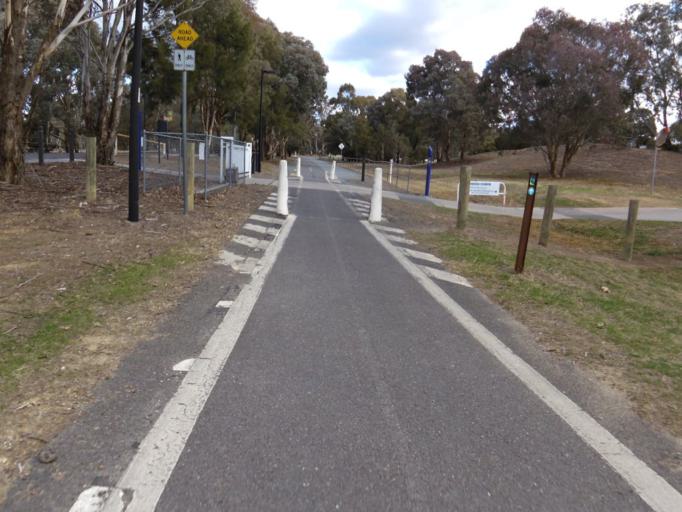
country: AU
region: Australian Capital Territory
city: Kaleen
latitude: -35.2490
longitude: 149.1051
